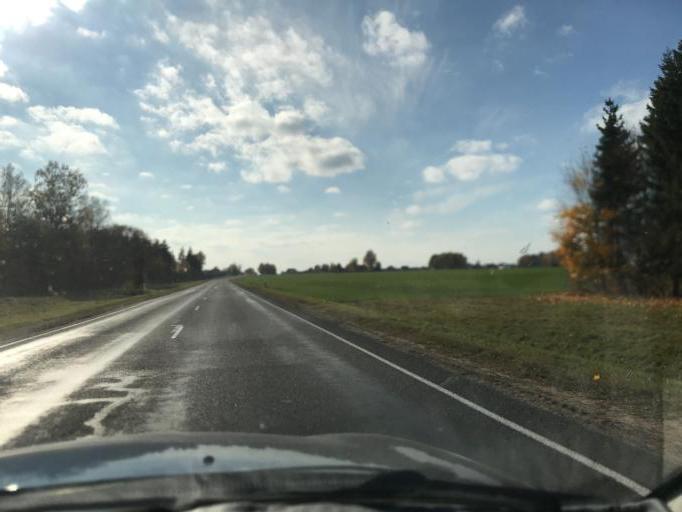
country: BY
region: Grodnenskaya
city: Voranava
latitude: 54.1751
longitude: 25.3336
